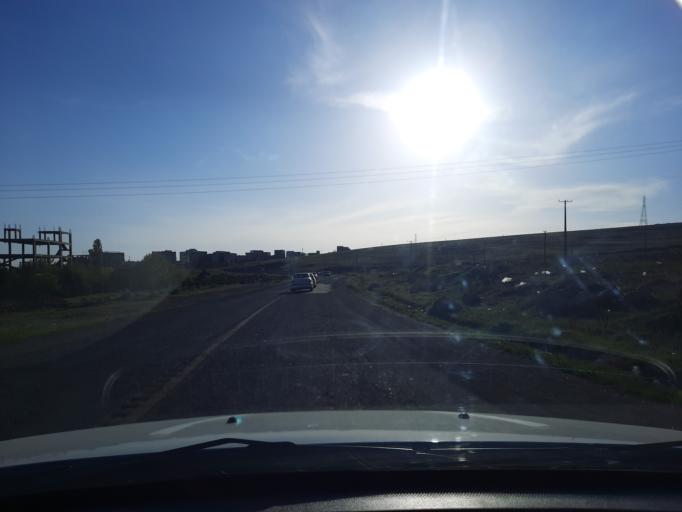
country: IR
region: Qazvin
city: Qazvin
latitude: 36.3373
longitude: 50.1567
